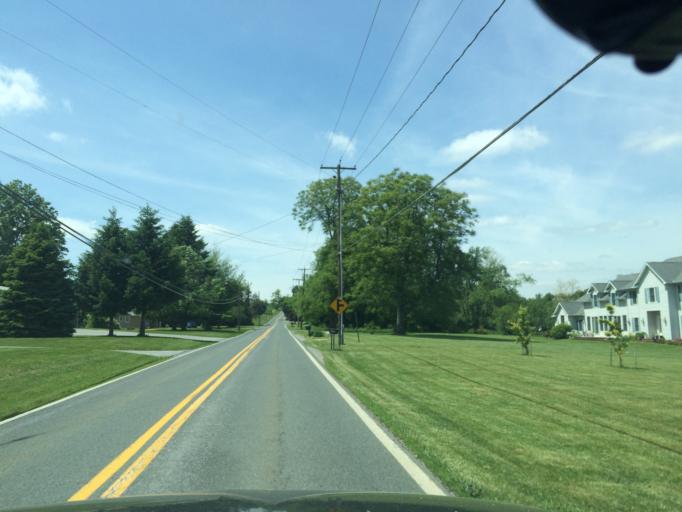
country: US
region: Maryland
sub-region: Carroll County
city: Westminster
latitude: 39.5104
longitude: -76.9536
